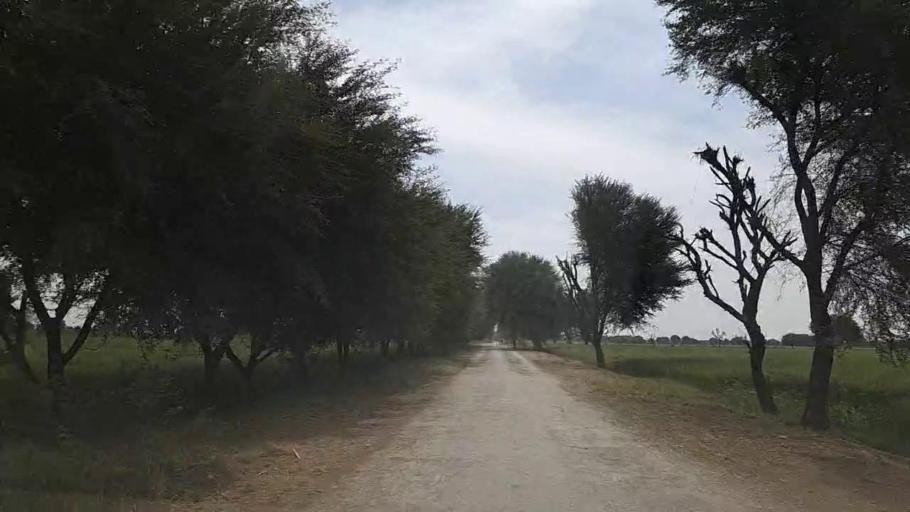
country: PK
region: Sindh
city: Samaro
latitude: 25.2873
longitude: 69.4538
